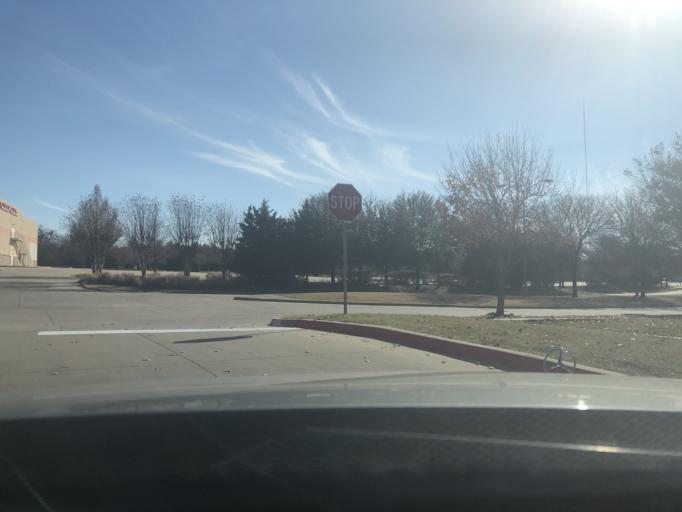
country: US
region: Texas
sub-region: Dallas County
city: Cedar Hill
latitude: 32.5926
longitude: -96.9514
